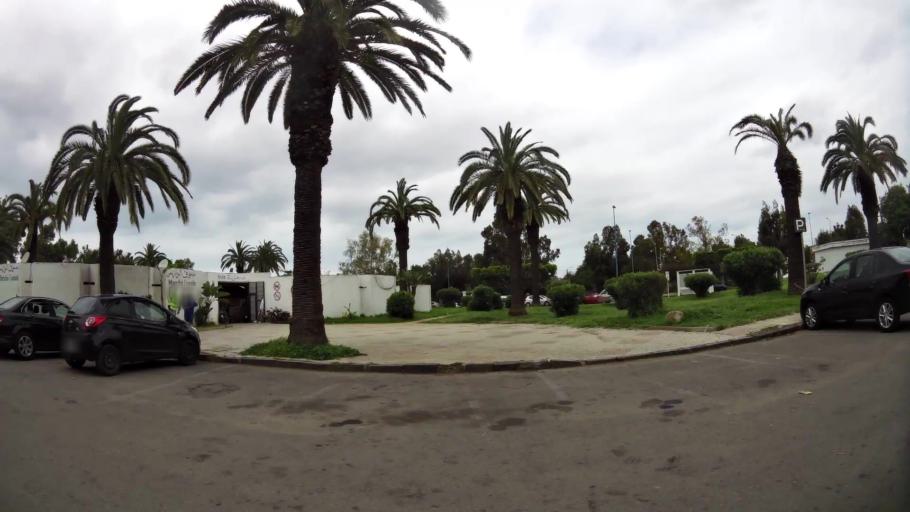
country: MA
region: Grand Casablanca
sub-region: Casablanca
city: Casablanca
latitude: 33.5566
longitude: -7.6348
